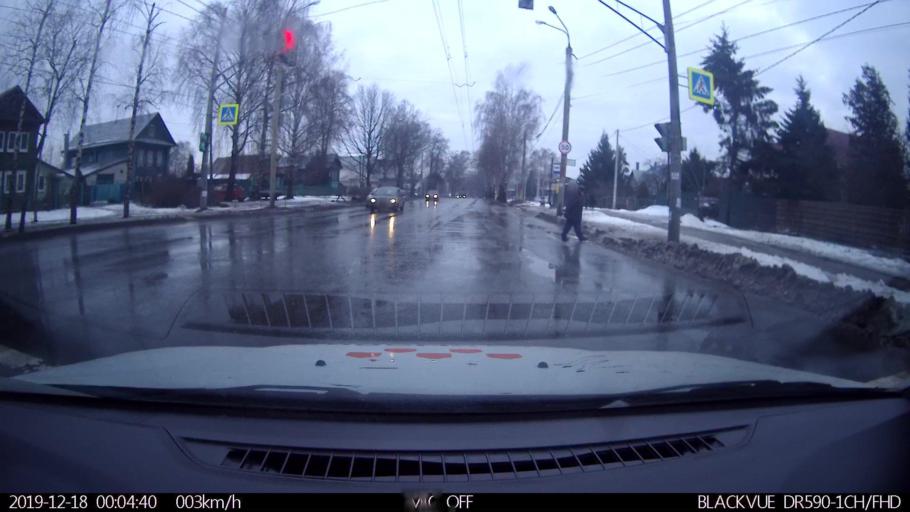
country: RU
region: Nizjnij Novgorod
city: Neklyudovo
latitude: 56.3659
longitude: 43.8476
